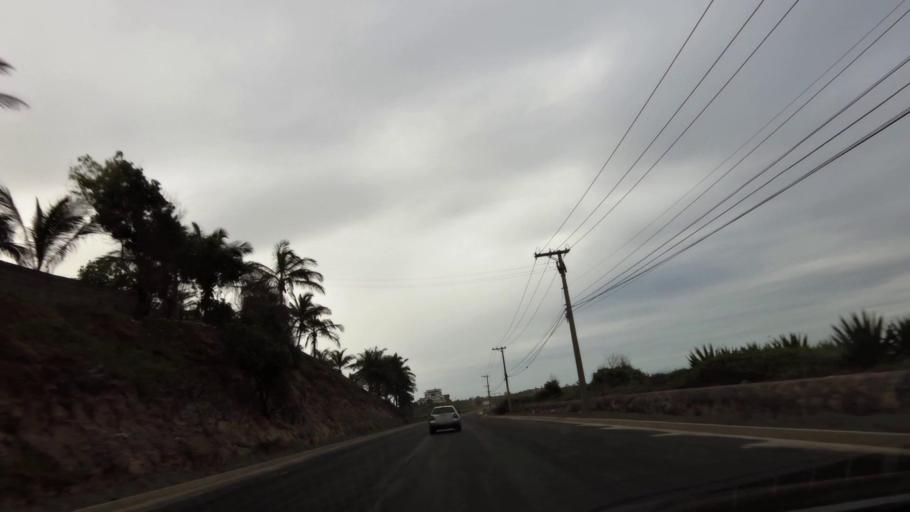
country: BR
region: Espirito Santo
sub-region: Guarapari
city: Guarapari
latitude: -20.7481
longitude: -40.5585
